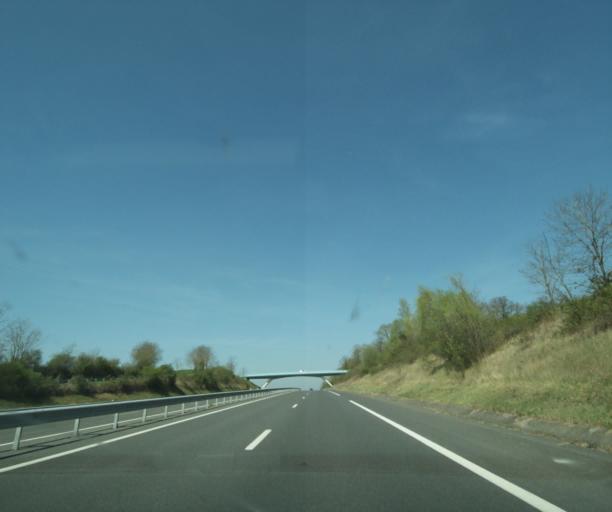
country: FR
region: Bourgogne
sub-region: Departement de la Nievre
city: Pouilly-sur-Loire
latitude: 47.2987
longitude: 2.9523
